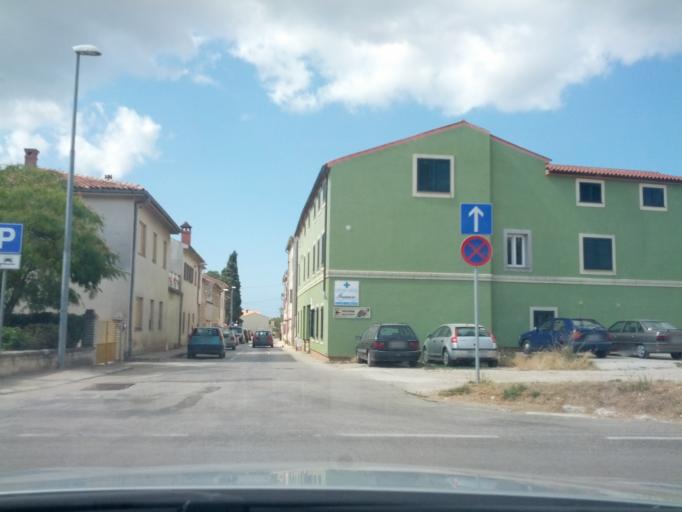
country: HR
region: Istarska
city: Vodnjan
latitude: 44.9571
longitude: 13.8452
